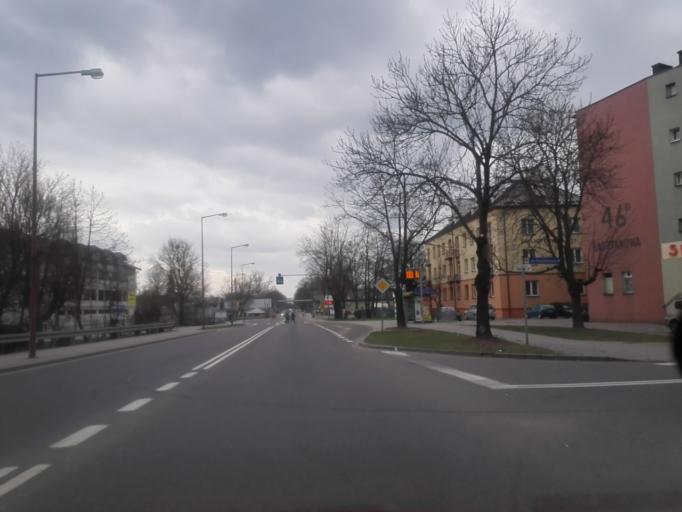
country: PL
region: Podlasie
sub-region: Powiat augustowski
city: Augustow
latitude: 53.8455
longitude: 22.9977
